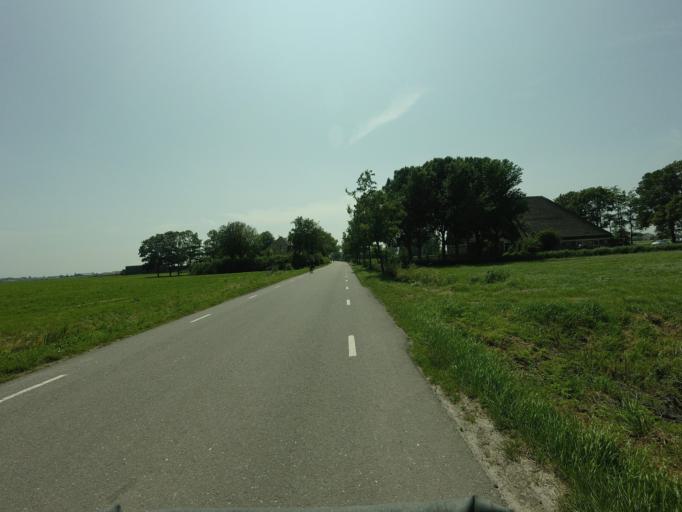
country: NL
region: North Holland
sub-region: Gemeente Opmeer
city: Opmeer
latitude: 52.6708
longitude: 4.9463
